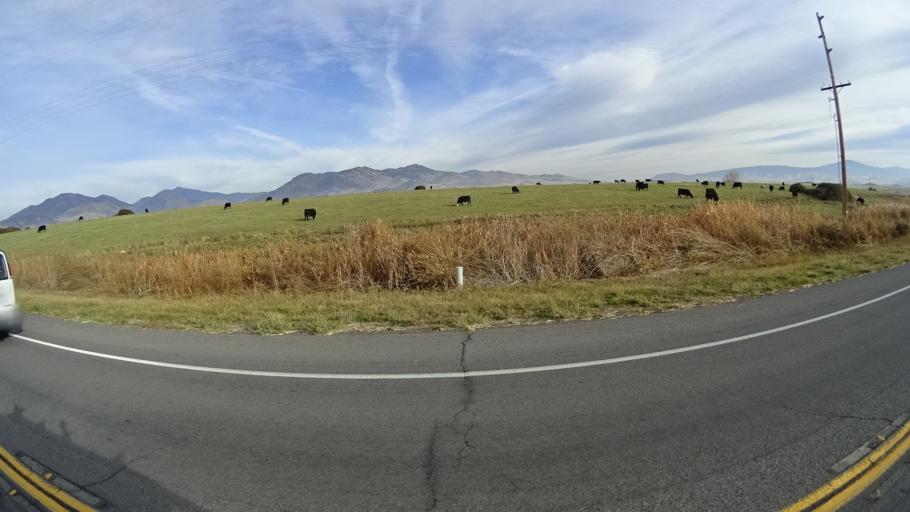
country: US
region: California
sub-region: Siskiyou County
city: Montague
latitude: 41.7290
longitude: -122.5714
